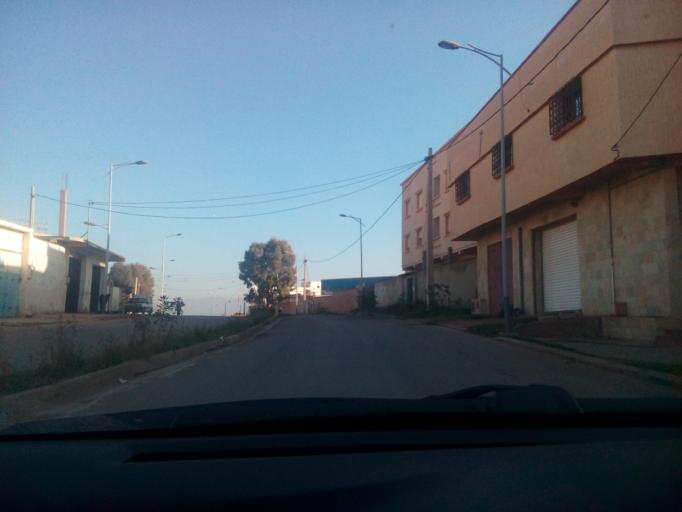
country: DZ
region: Oran
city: Bir el Djir
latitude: 35.7594
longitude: -0.5352
